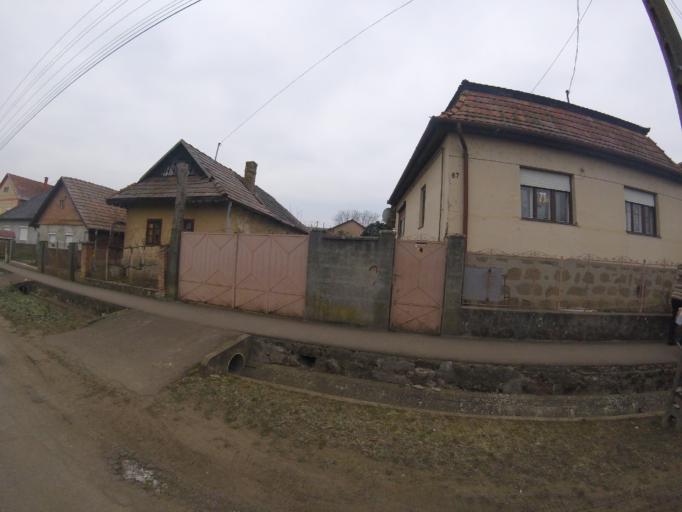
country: HU
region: Nograd
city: Paszto
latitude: 47.9564
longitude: 19.6884
